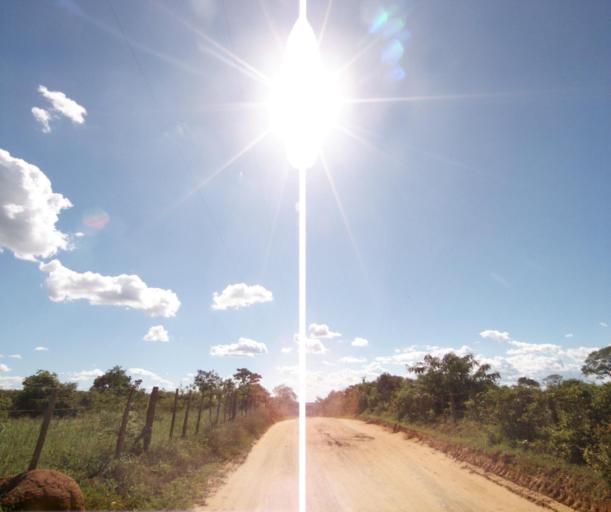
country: BR
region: Bahia
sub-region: Carinhanha
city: Carinhanha
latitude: -14.1804
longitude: -44.5145
